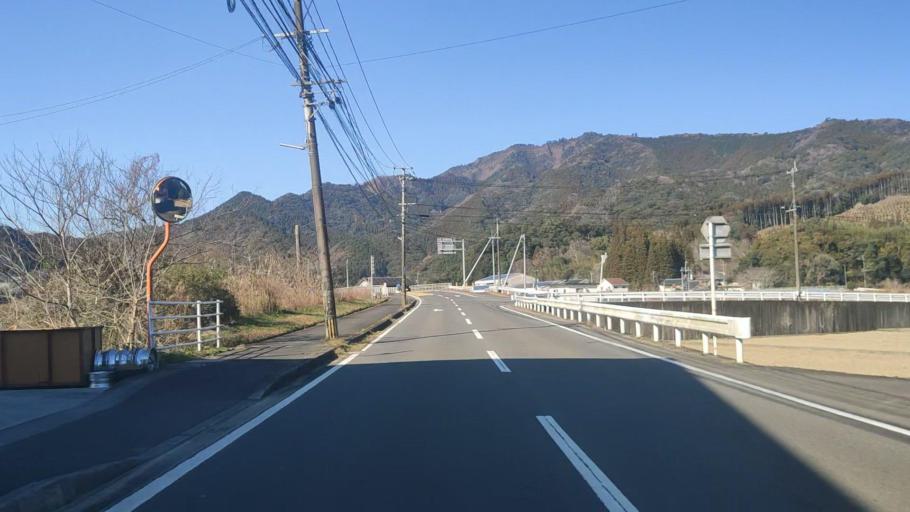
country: JP
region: Oita
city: Saiki
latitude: 32.9776
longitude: 131.8513
